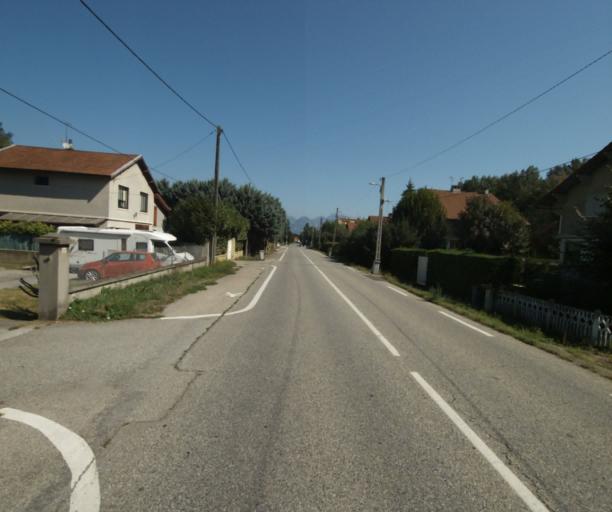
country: FR
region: Rhone-Alpes
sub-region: Departement de l'Isere
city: Claix
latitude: 45.1136
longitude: 5.6898
